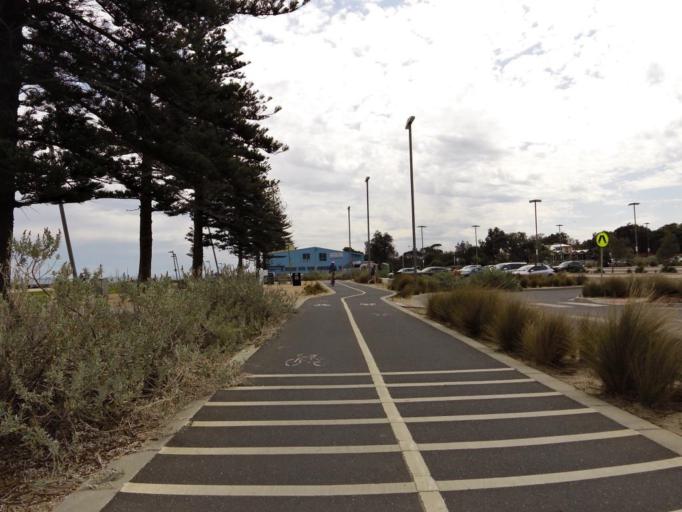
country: AU
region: Victoria
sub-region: Port Phillip
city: Elwood
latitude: -37.8890
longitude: 144.9842
